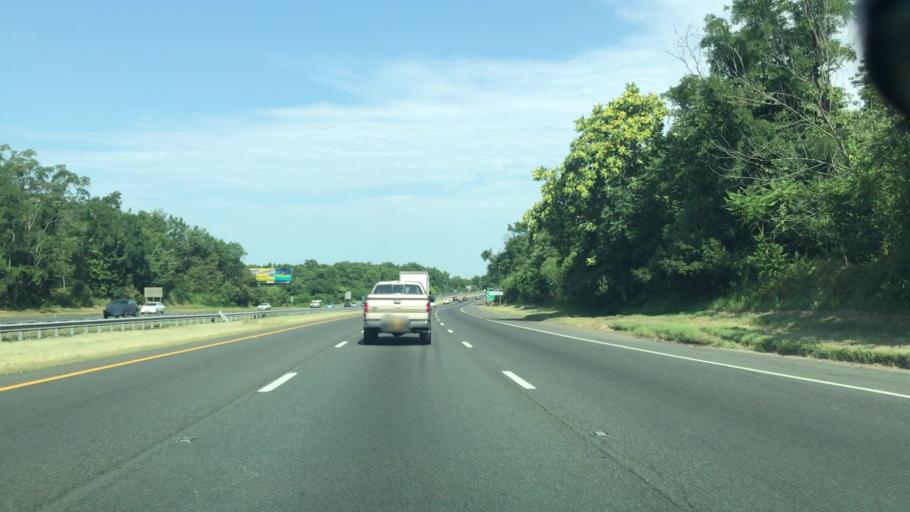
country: US
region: New Jersey
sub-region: Somerset County
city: South Bound Brook
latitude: 40.5400
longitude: -74.5230
